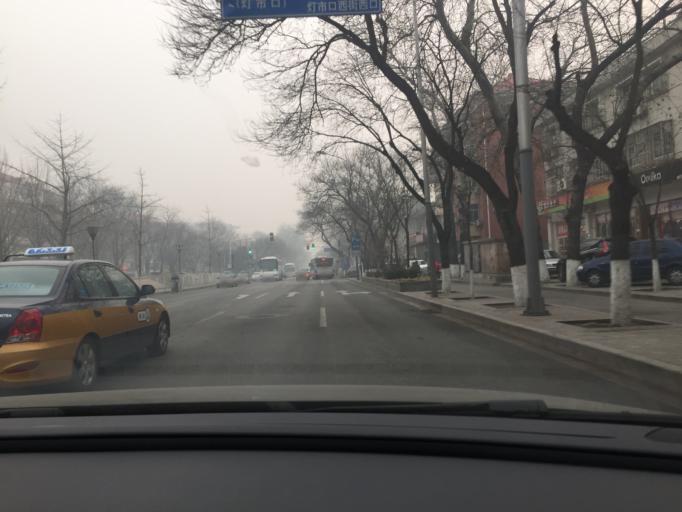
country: CN
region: Beijing
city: Jingshan
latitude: 39.9179
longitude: 116.4002
